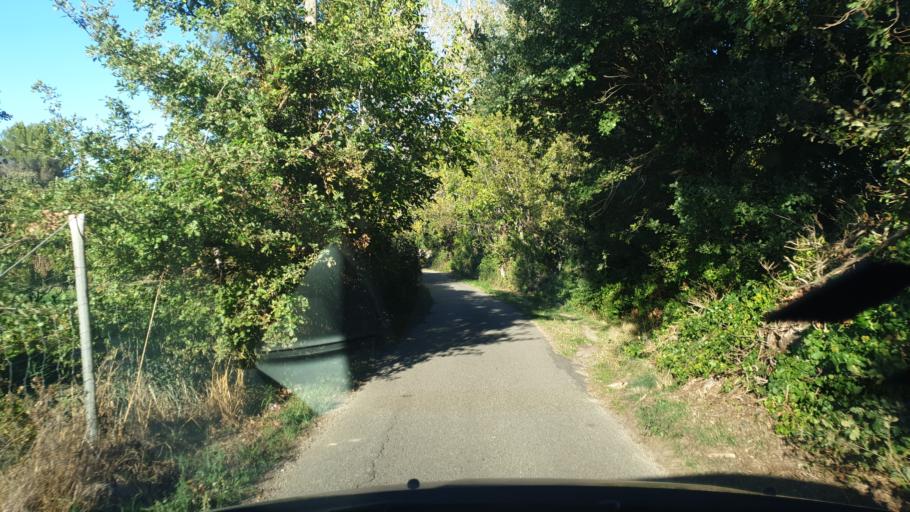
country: FR
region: Provence-Alpes-Cote d'Azur
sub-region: Departement du Vaucluse
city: Loriol-du-Comtat
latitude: 44.0571
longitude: 5.0051
